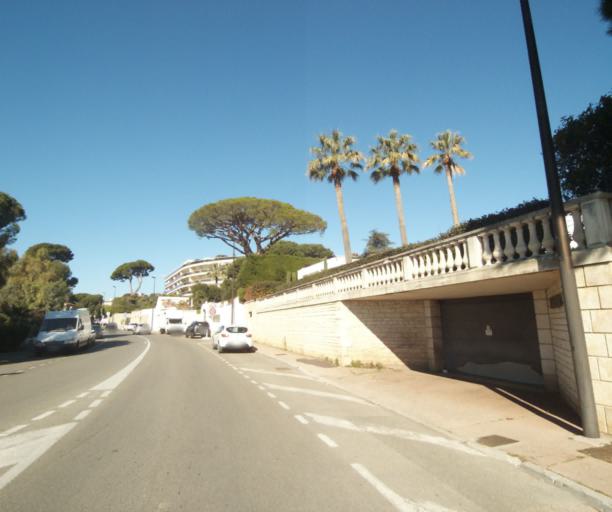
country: FR
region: Provence-Alpes-Cote d'Azur
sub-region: Departement des Alpes-Maritimes
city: Antibes
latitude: 43.5630
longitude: 7.1176
